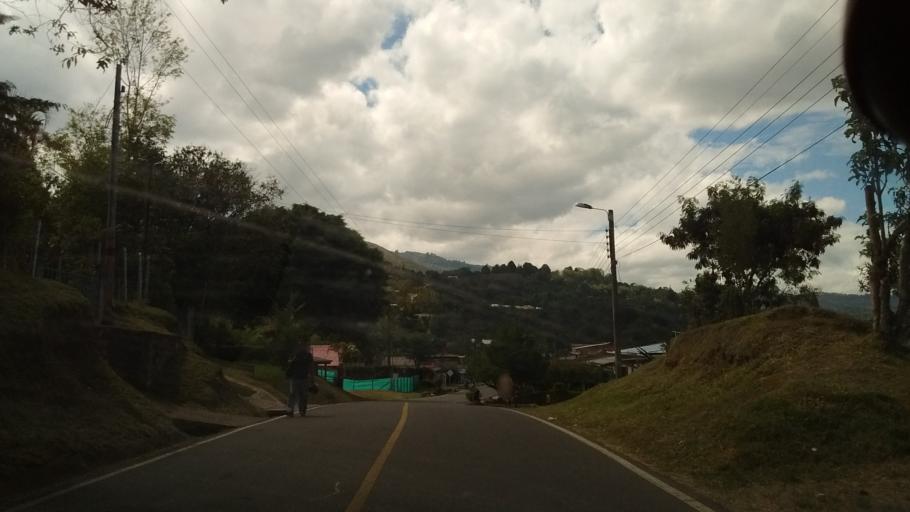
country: CO
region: Cauca
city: Cajibio
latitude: 2.6285
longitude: -76.5186
